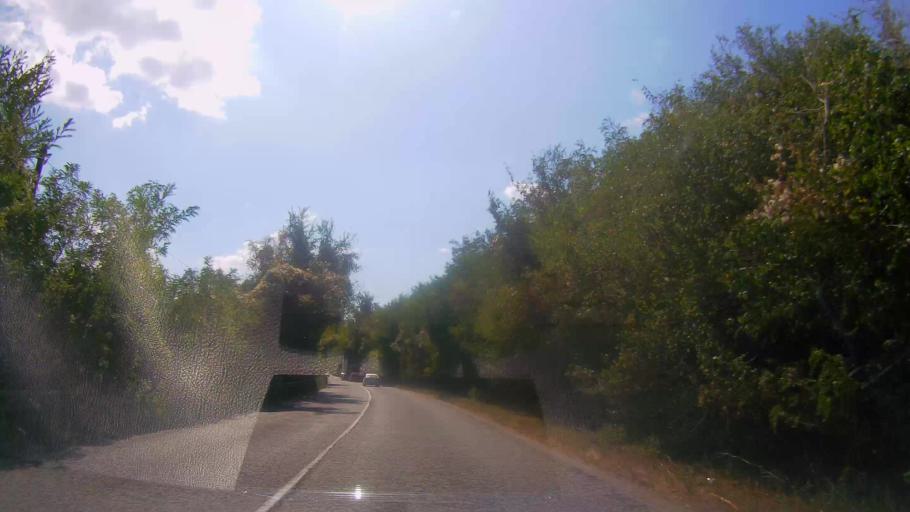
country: BG
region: Veliko Turnovo
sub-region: Obshtina Polski Trumbesh
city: Polski Trumbesh
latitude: 43.4368
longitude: 25.6544
